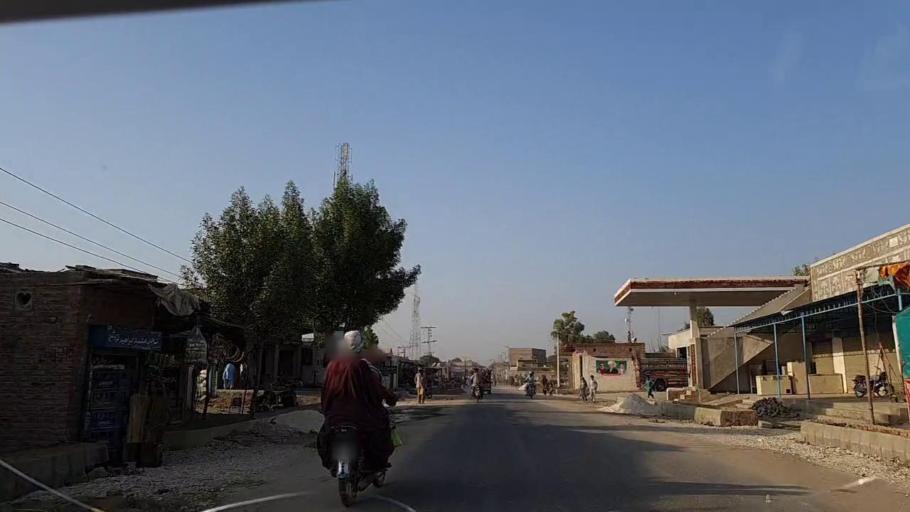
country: PK
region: Sindh
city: Rustam jo Goth
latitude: 27.9623
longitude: 68.8060
